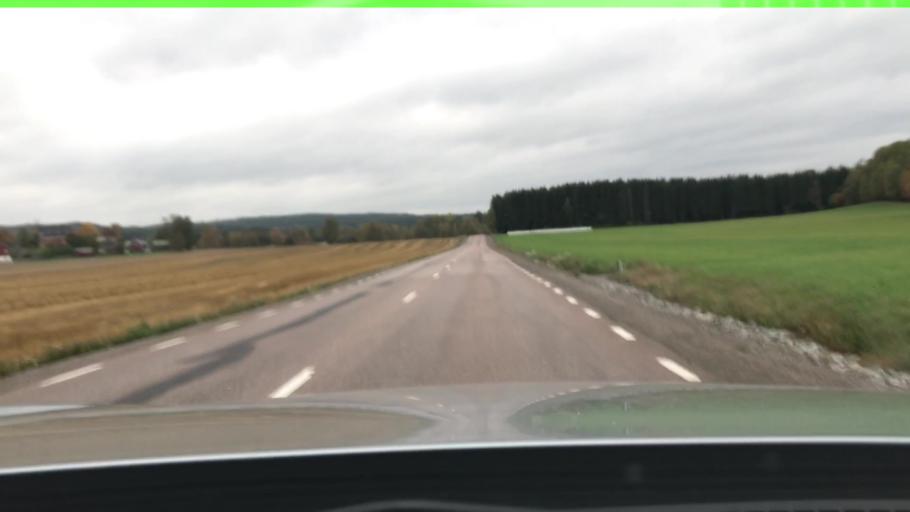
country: SE
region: Vaermland
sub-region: Eda Kommun
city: Amotfors
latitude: 59.7361
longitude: 12.1990
